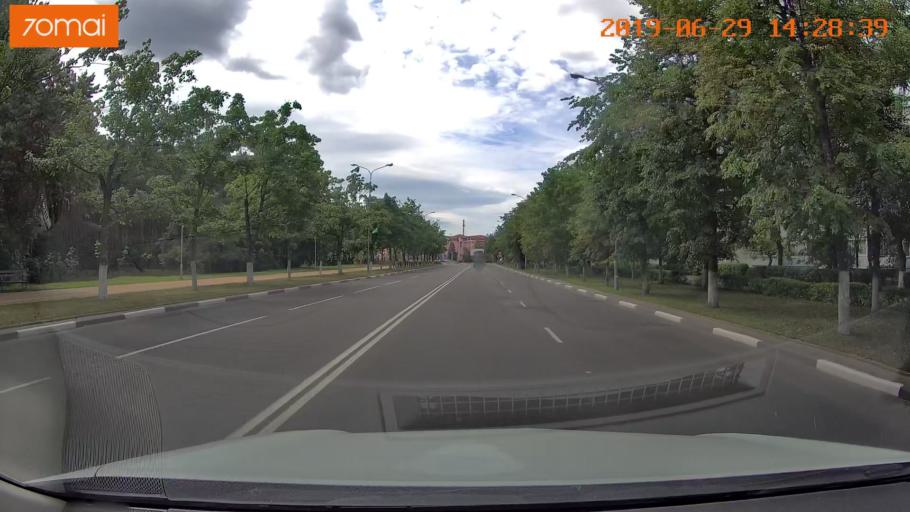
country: BY
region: Minsk
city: Salihorsk
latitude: 52.7830
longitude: 27.5299
